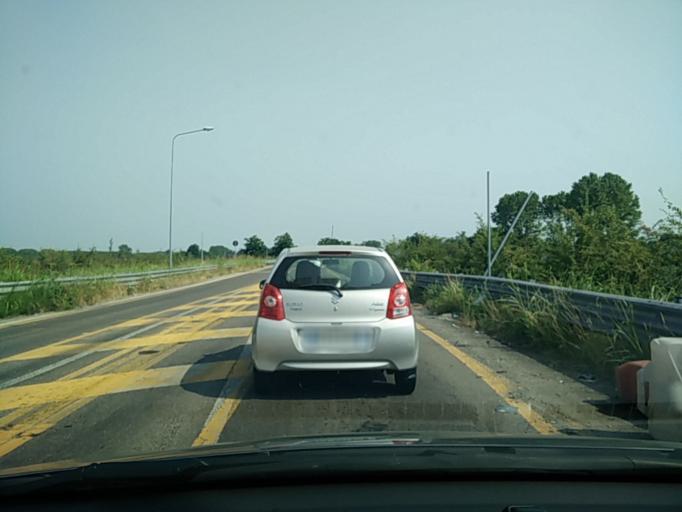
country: IT
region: Lombardy
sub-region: Provincia di Pavia
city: Valle Salimbene
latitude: 45.1505
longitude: 9.2276
